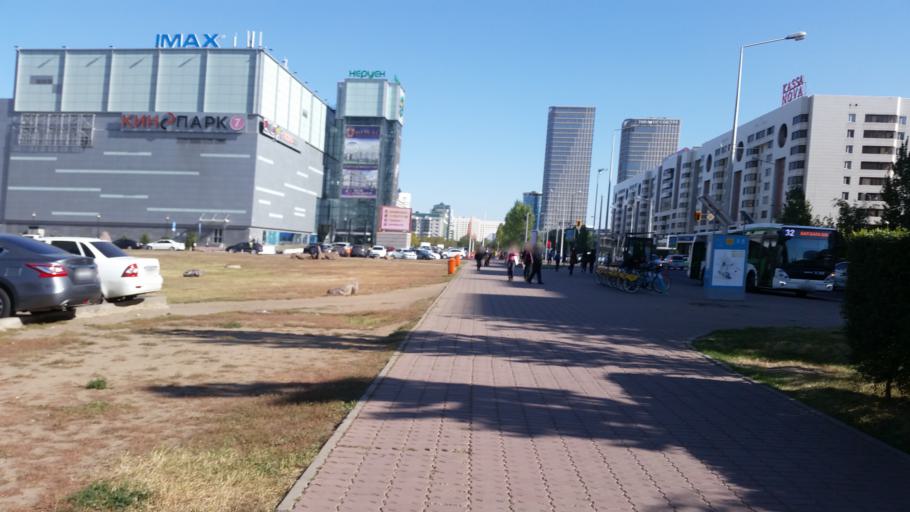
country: KZ
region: Astana Qalasy
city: Astana
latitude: 51.1273
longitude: 71.4225
